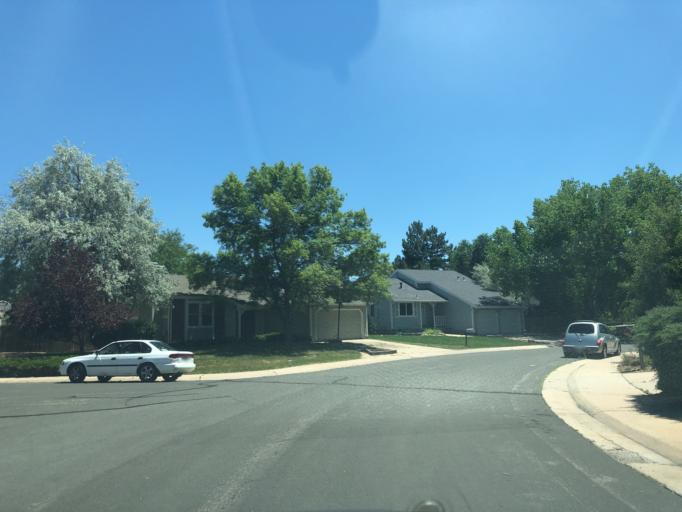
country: US
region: Colorado
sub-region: Arapahoe County
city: Dove Valley
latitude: 39.6186
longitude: -104.7744
